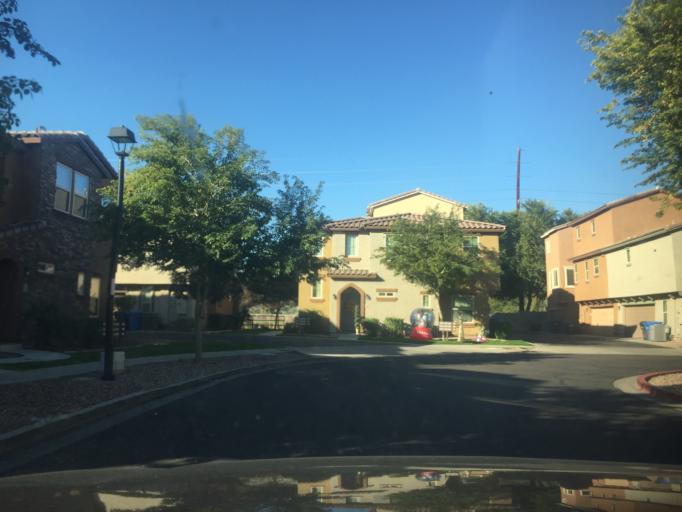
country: US
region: Arizona
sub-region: Maricopa County
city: Tolleson
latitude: 33.4689
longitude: -112.2284
